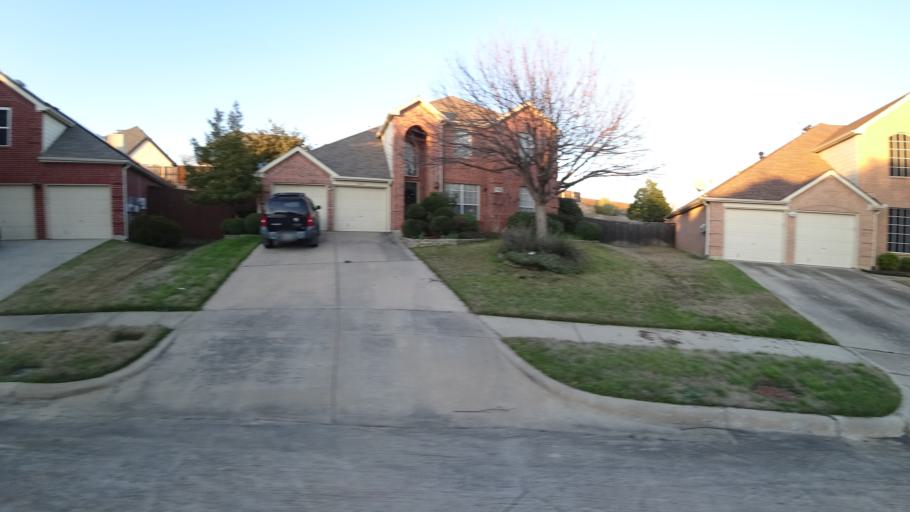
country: US
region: Texas
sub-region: Dallas County
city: Coppell
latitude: 32.9929
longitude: -96.9951
